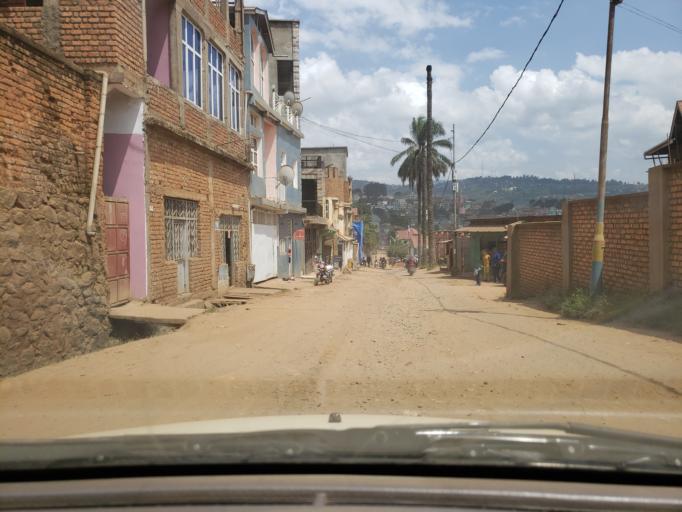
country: CD
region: South Kivu
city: Bukavu
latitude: -2.4983
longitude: 28.8679
